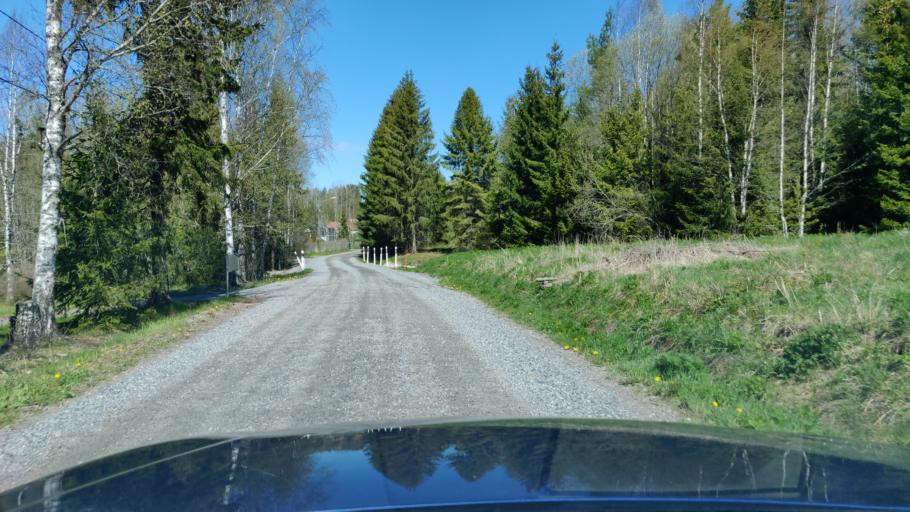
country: FI
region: Uusimaa
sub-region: Helsinki
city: Nurmijaervi
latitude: 60.3590
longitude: 24.7566
